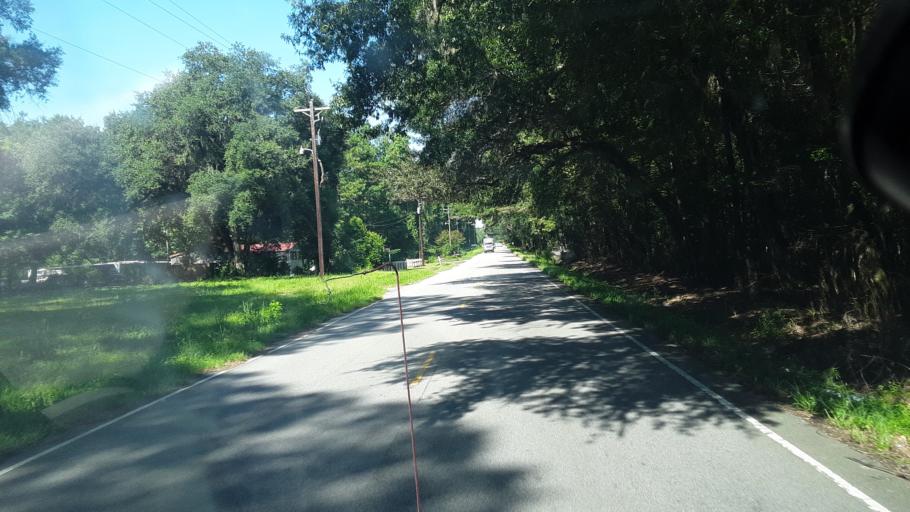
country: US
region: South Carolina
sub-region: Jasper County
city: Ridgeland
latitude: 32.5888
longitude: -80.9321
